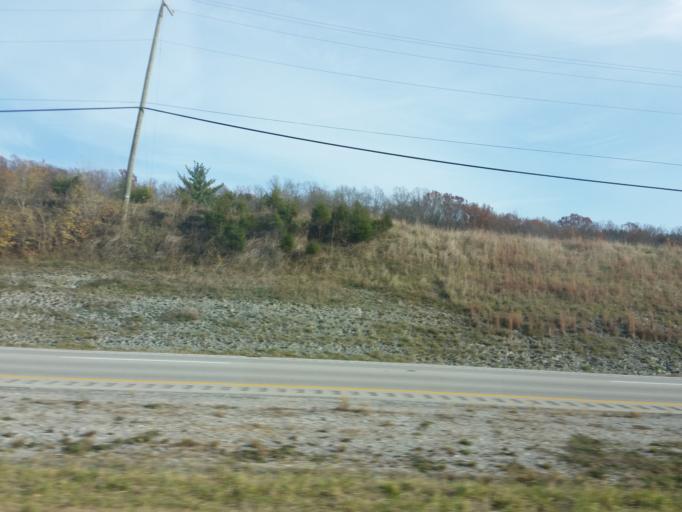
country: US
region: Kentucky
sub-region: Campbell County
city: Claryville
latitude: 38.8728
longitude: -84.3938
